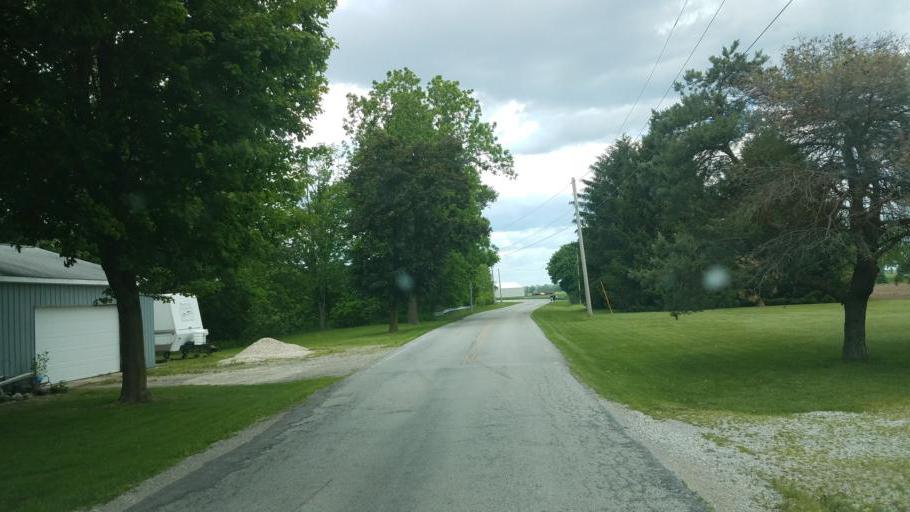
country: US
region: Ohio
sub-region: Huron County
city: Monroeville
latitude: 41.2587
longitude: -82.6794
